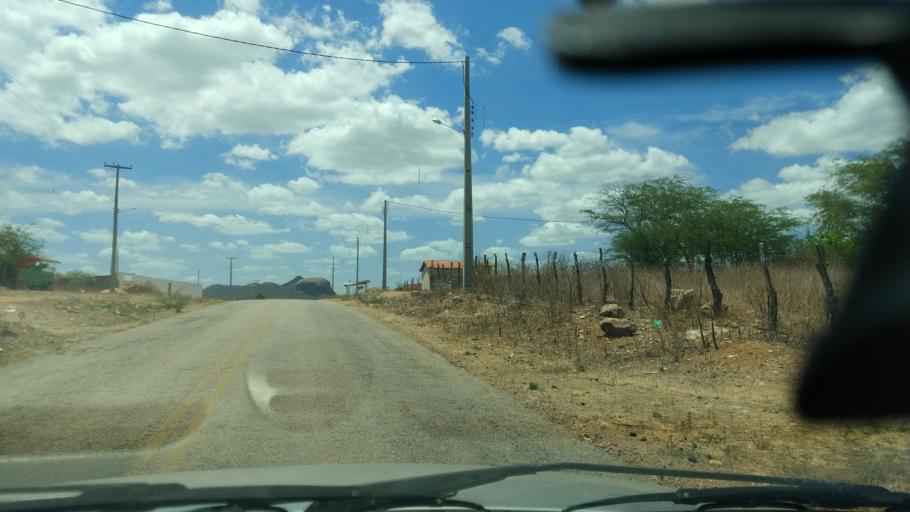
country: BR
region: Rio Grande do Norte
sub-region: Sao Paulo Do Potengi
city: Sao Paulo do Potengi
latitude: -5.9671
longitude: -35.8920
